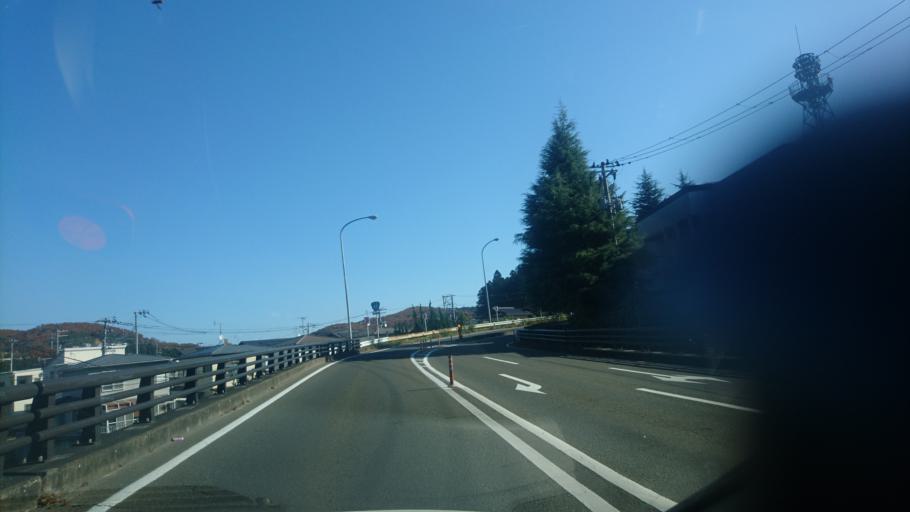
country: JP
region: Miyagi
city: Sendai
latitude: 38.2627
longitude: 140.8114
